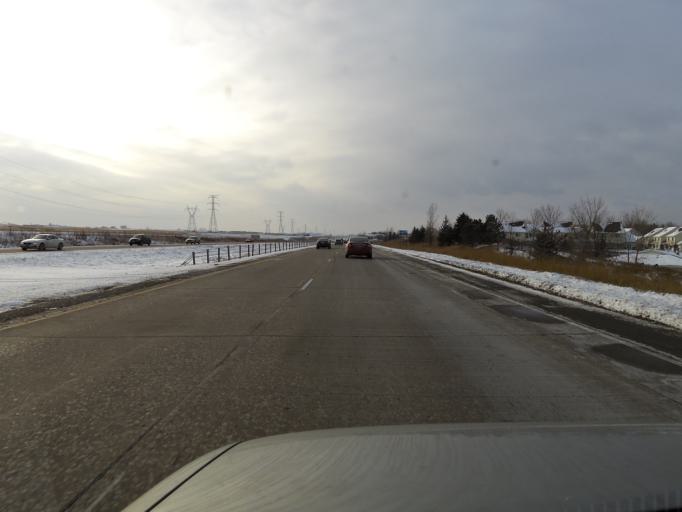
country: US
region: Minnesota
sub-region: Scott County
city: Shakopee
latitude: 44.7813
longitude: -93.4775
